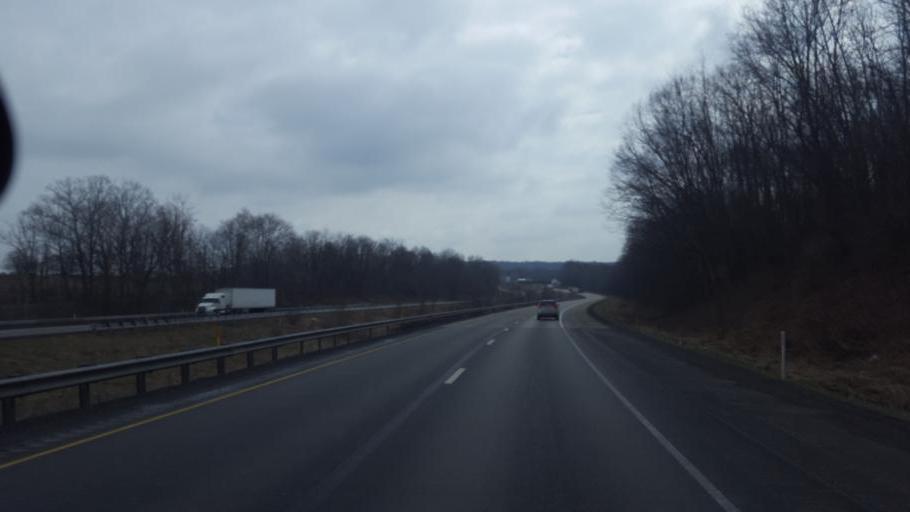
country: US
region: Pennsylvania
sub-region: Lawrence County
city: New Wilmington
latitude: 41.1846
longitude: -80.3251
